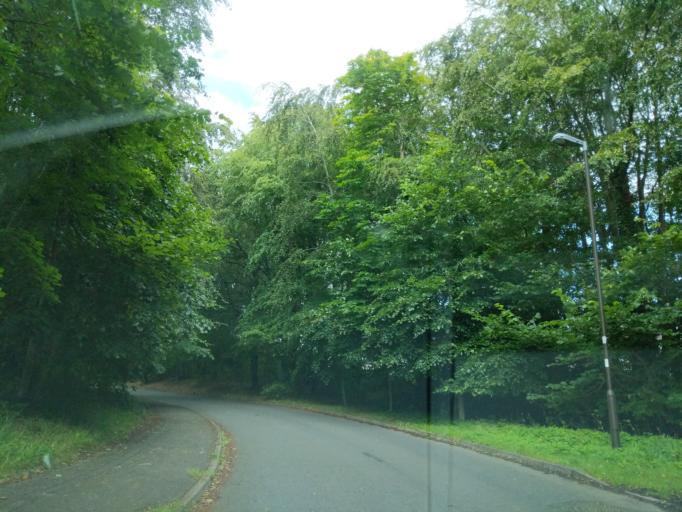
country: GB
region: Scotland
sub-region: Midlothian
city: Loanhead
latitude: 55.8743
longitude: -3.1473
